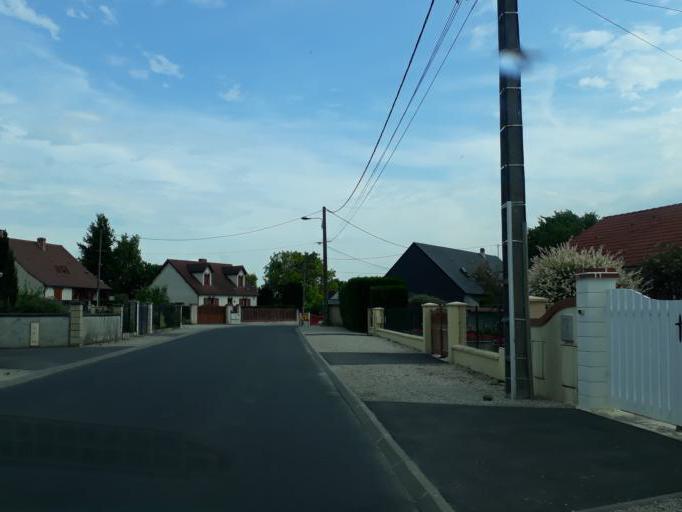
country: FR
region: Centre
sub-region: Departement du Loiret
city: Ingre
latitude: 47.9256
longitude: 1.8198
